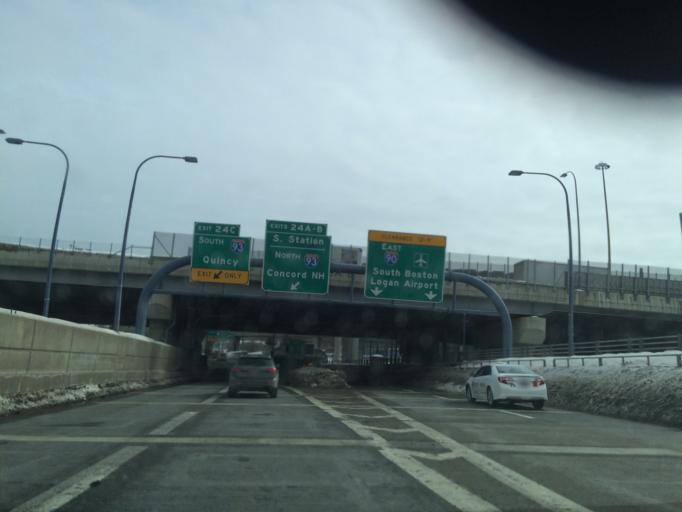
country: US
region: Massachusetts
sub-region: Suffolk County
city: Boston
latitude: 42.3465
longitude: -71.0617
